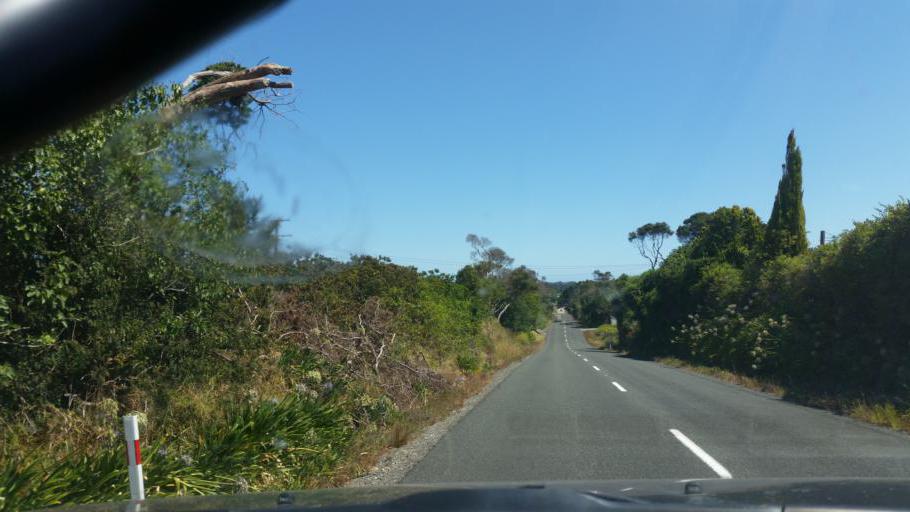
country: NZ
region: Northland
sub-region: Kaipara District
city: Dargaville
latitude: -36.0118
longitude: 173.9377
